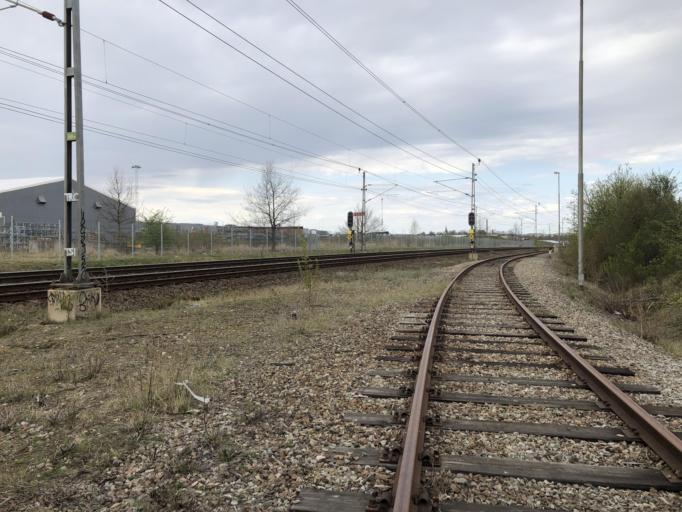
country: SE
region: Skane
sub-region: Malmo
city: Tygelsjo
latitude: 55.5540
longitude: 13.0346
